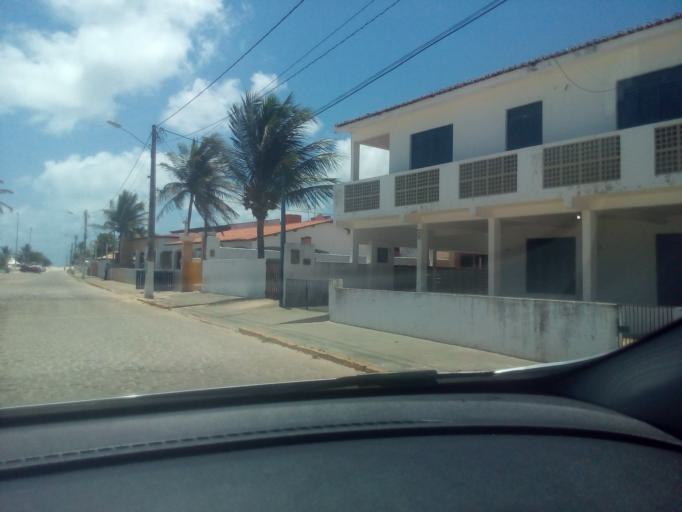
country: BR
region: Rio Grande do Norte
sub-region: Parnamirim
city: Parnamirim
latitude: -5.9698
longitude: -35.1280
